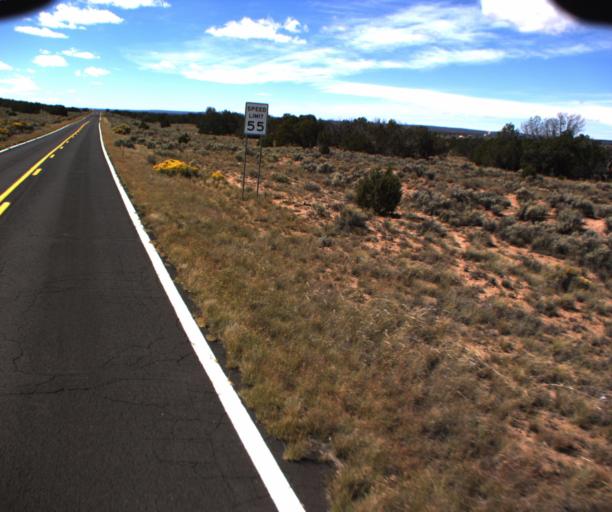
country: US
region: Arizona
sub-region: Apache County
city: Houck
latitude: 34.9086
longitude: -109.2273
